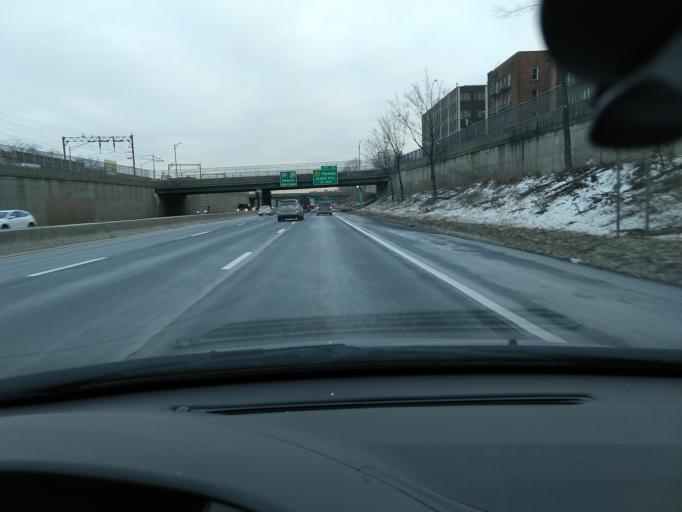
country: US
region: New Jersey
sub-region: Essex County
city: East Orange
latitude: 40.7637
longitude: -74.2171
